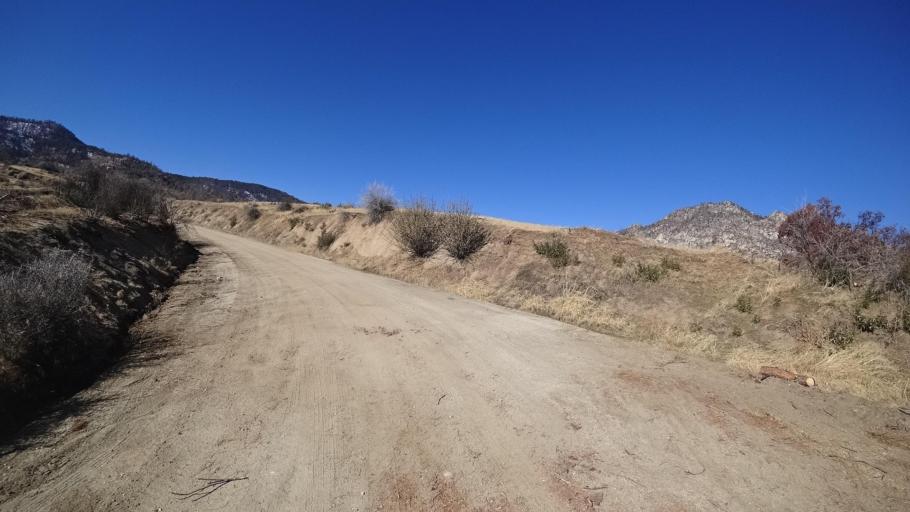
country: US
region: California
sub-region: Kern County
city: Alta Sierra
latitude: 35.7157
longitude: -118.5148
